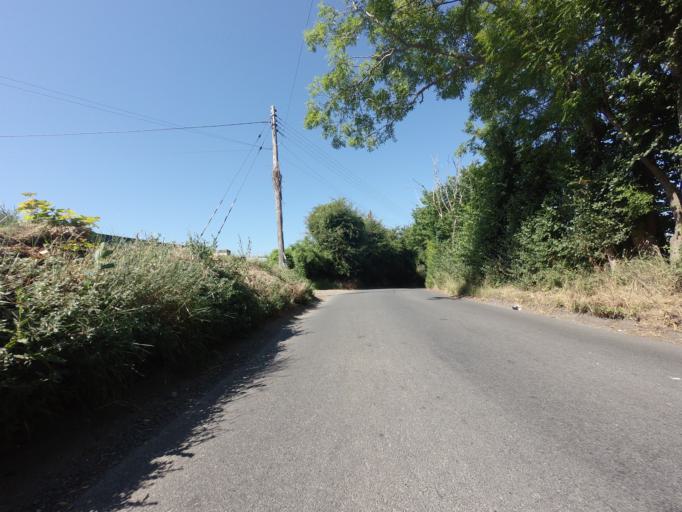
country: GB
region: England
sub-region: Kent
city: Dartford
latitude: 51.4131
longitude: 0.2166
